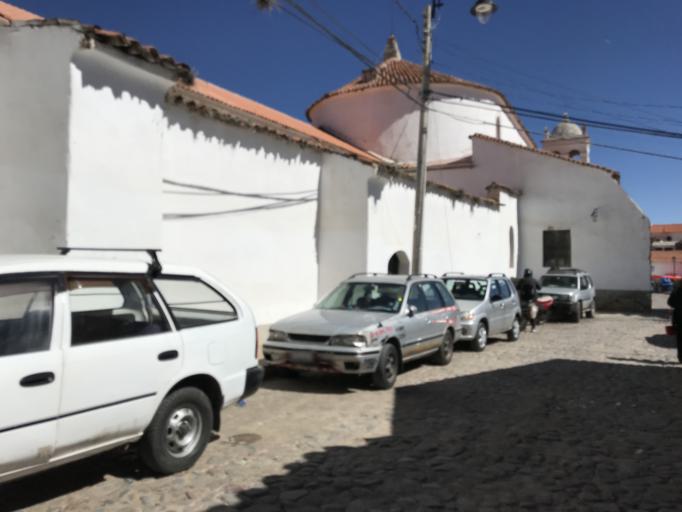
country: BO
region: Chuquisaca
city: Sucre
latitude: -19.0548
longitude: -65.2527
